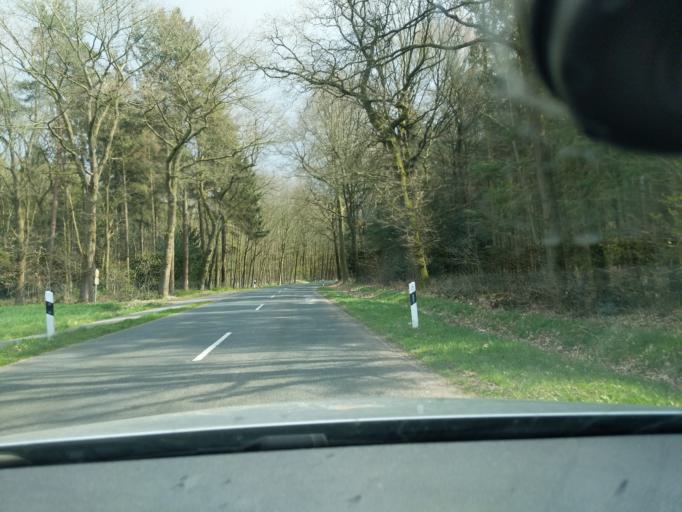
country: DE
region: Lower Saxony
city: Dollern
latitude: 53.5128
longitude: 9.5429
